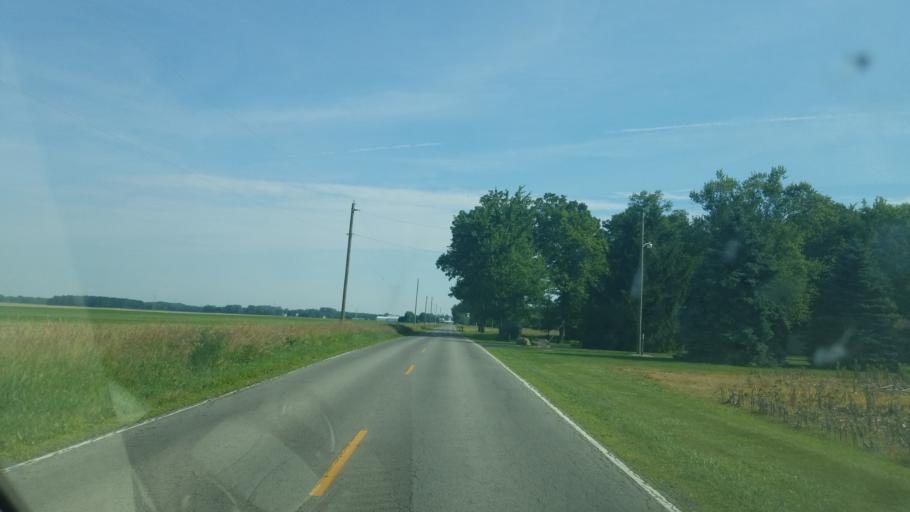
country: US
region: Ohio
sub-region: Hancock County
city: Findlay
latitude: 41.0126
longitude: -83.5881
